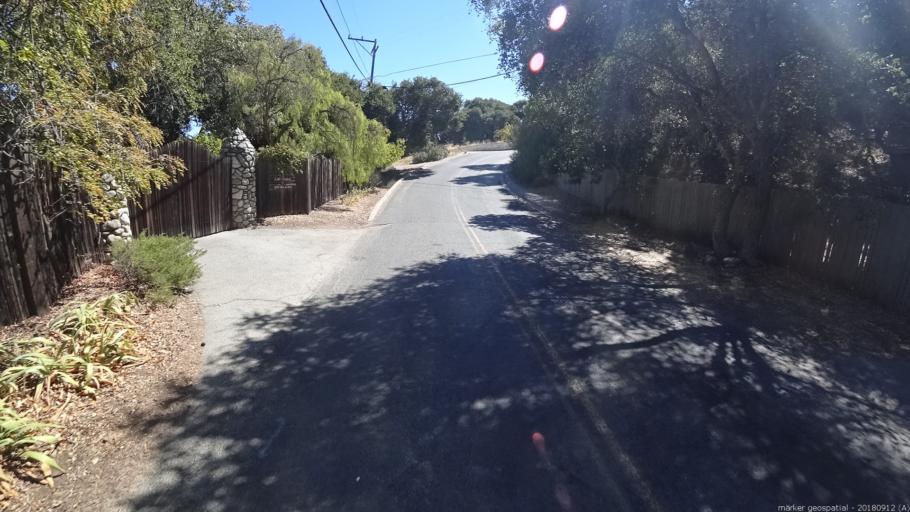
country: US
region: California
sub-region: Monterey County
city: Carmel Valley Village
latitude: 36.4702
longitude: -121.7281
